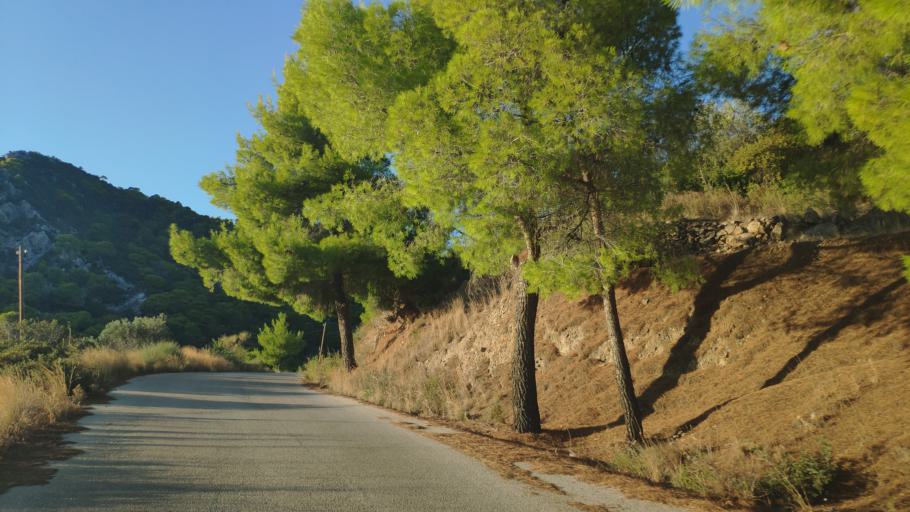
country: GR
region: Attica
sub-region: Nomos Piraios
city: Megalochori
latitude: 37.6098
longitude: 23.3289
